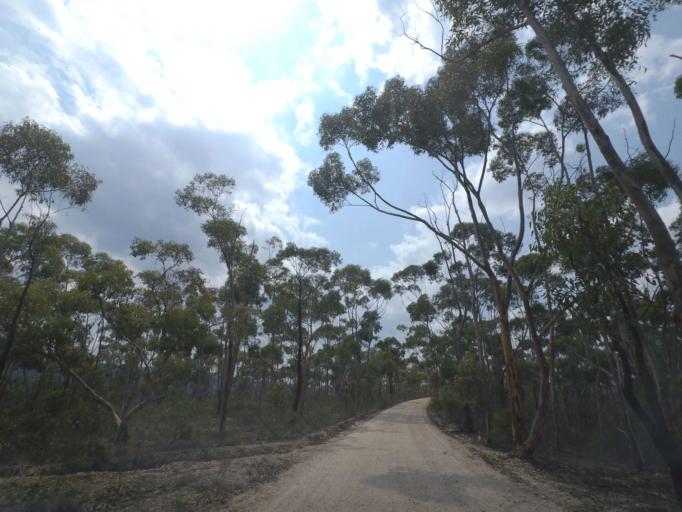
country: AU
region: Victoria
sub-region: Moorabool
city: Bacchus Marsh
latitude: -37.5852
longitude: 144.4356
